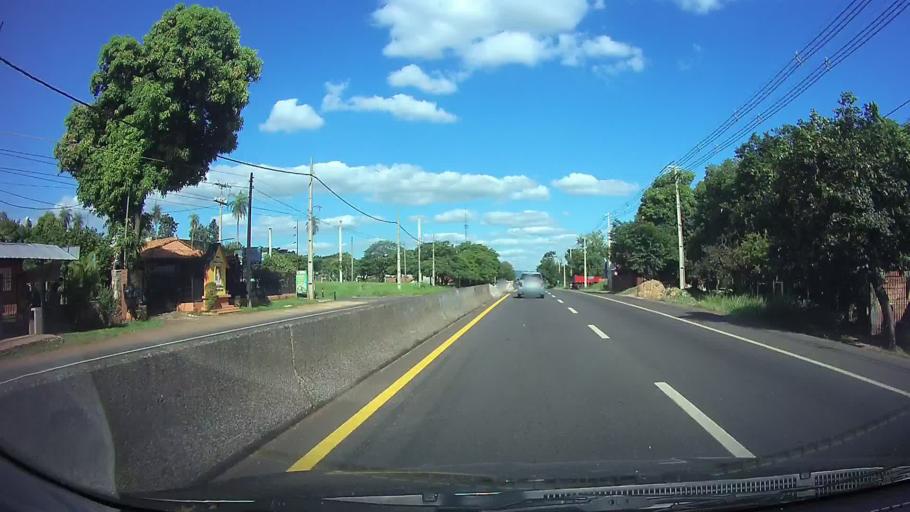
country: PY
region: Central
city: Itaugua
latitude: -25.4002
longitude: -57.3220
